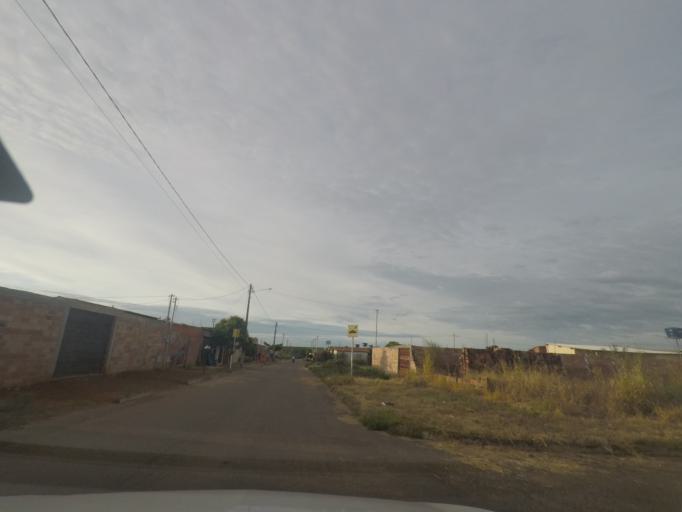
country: BR
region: Goias
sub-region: Trindade
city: Trindade
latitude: -16.7237
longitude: -49.4375
